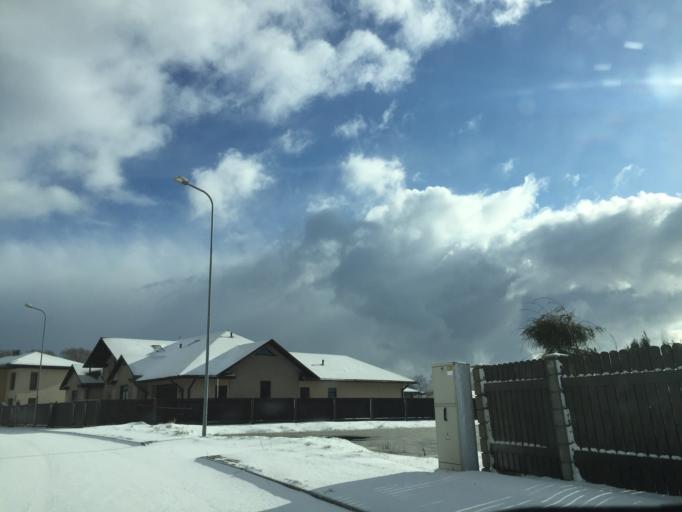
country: LV
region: Ventspils
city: Ventspils
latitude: 57.3773
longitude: 21.5623
